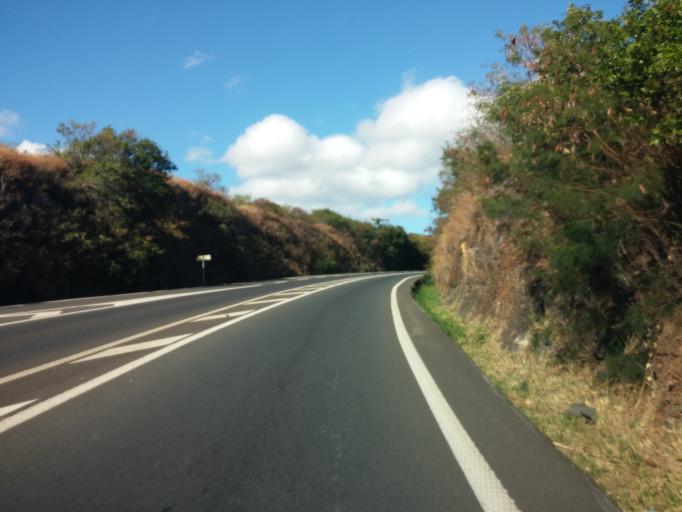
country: RE
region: Reunion
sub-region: Reunion
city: Saint-Paul
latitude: -21.0285
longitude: 55.2742
